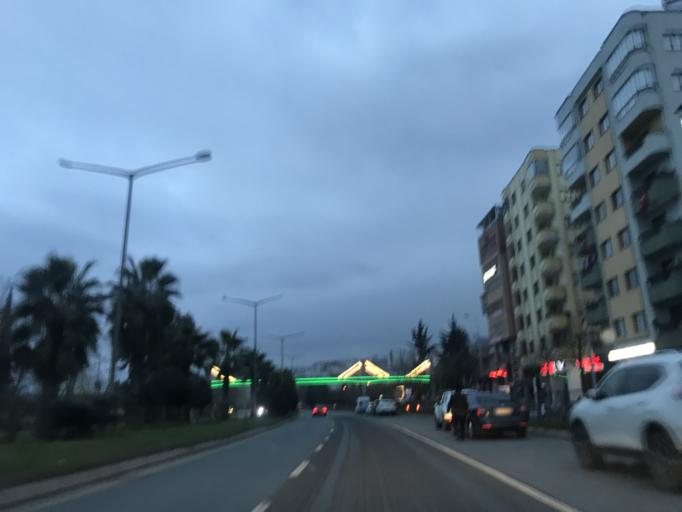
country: TR
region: Trabzon
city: Akcaabat
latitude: 41.0249
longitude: 39.5657
